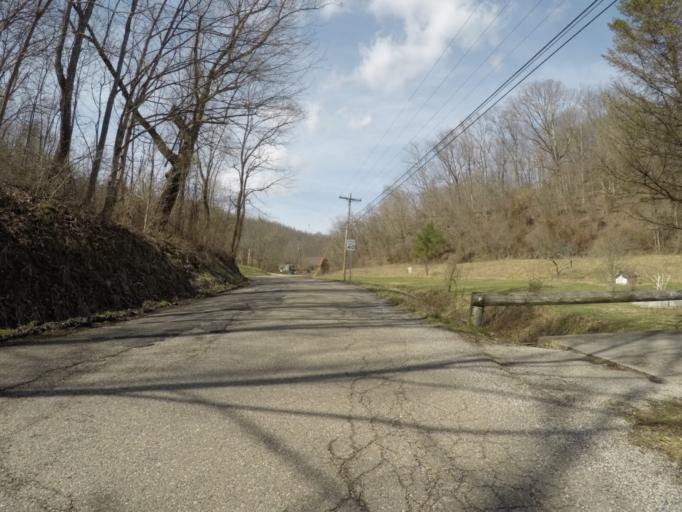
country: US
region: Ohio
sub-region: Lawrence County
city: Burlington
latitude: 38.4804
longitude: -82.5255
